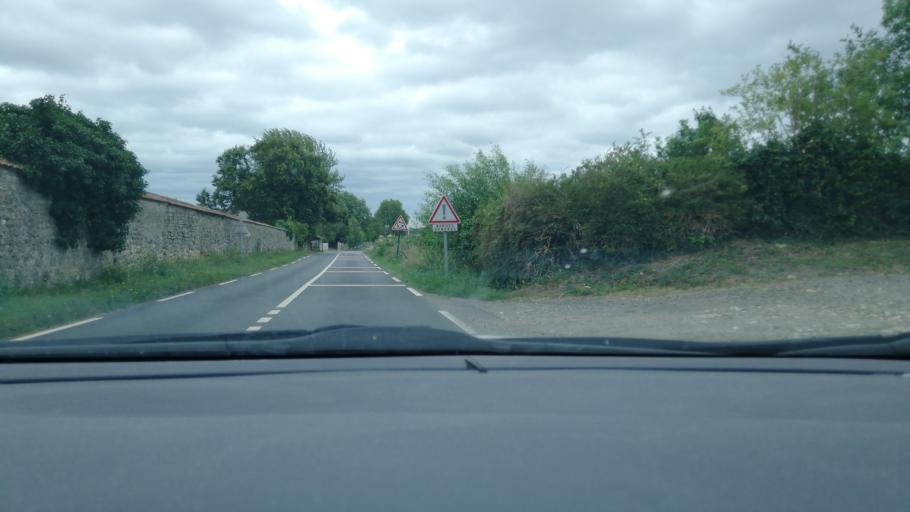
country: FR
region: Ile-de-France
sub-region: Departement du Val-d'Oise
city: Ennery
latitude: 49.1002
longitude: 2.1346
